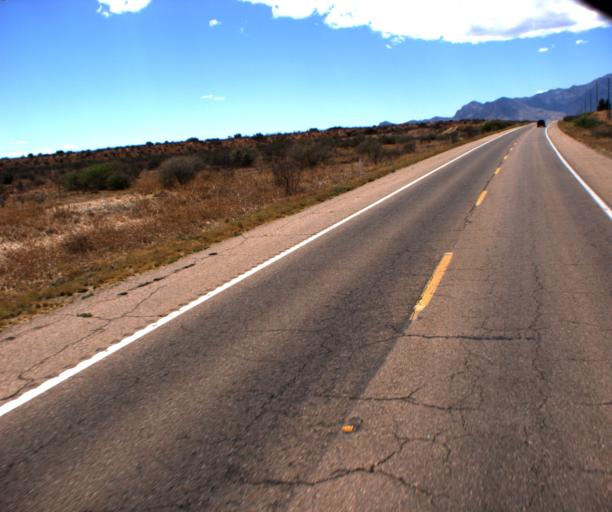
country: US
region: Arizona
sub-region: Cochise County
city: Naco
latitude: 31.3801
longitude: -110.0778
